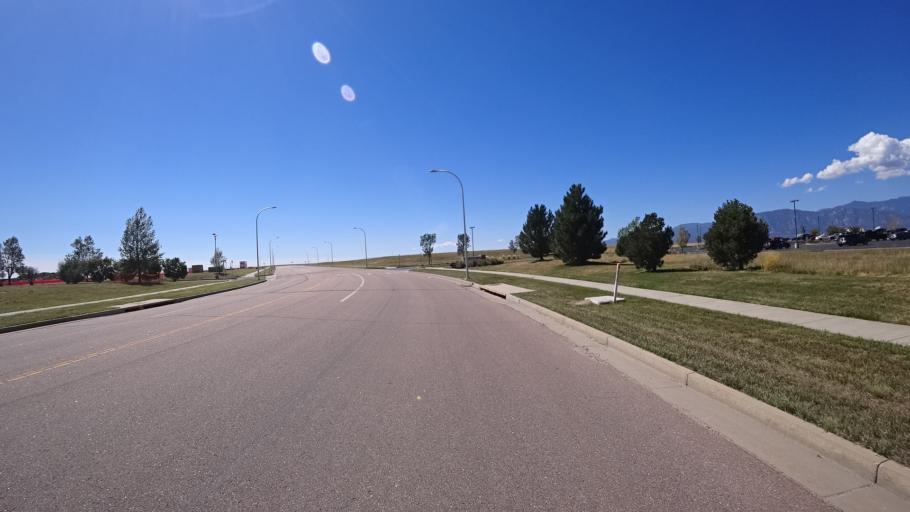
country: US
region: Colorado
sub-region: El Paso County
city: Security-Widefield
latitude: 38.7788
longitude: -104.6998
